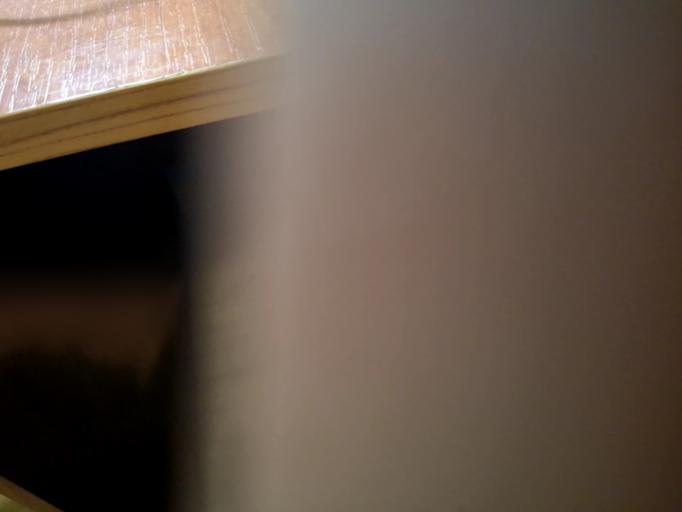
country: RU
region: Sverdlovsk
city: Krasnotur'insk
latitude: 59.9016
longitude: 60.2117
